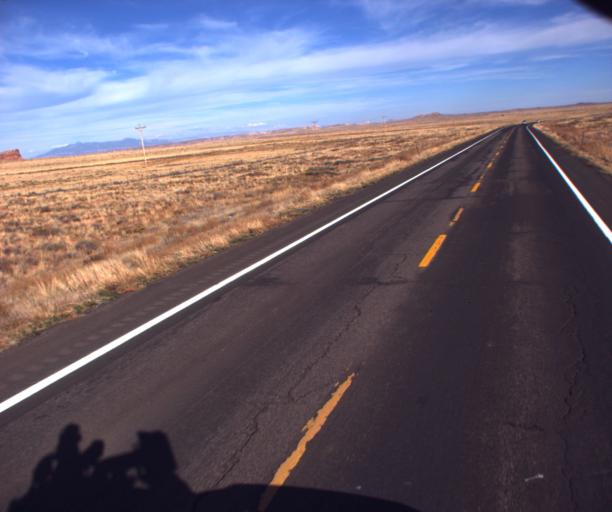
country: US
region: Arizona
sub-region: Apache County
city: Lukachukai
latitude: 36.9585
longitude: -109.3131
